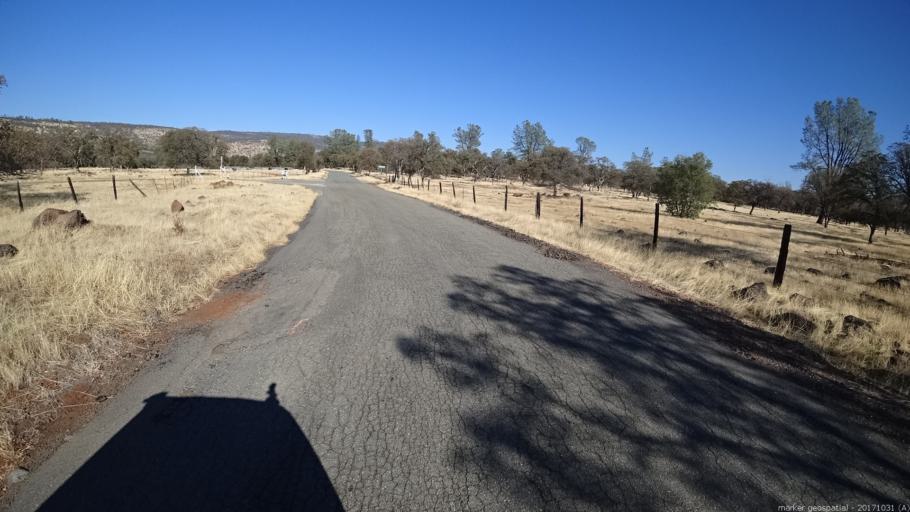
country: US
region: California
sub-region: Shasta County
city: Shingletown
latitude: 40.4260
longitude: -121.9811
